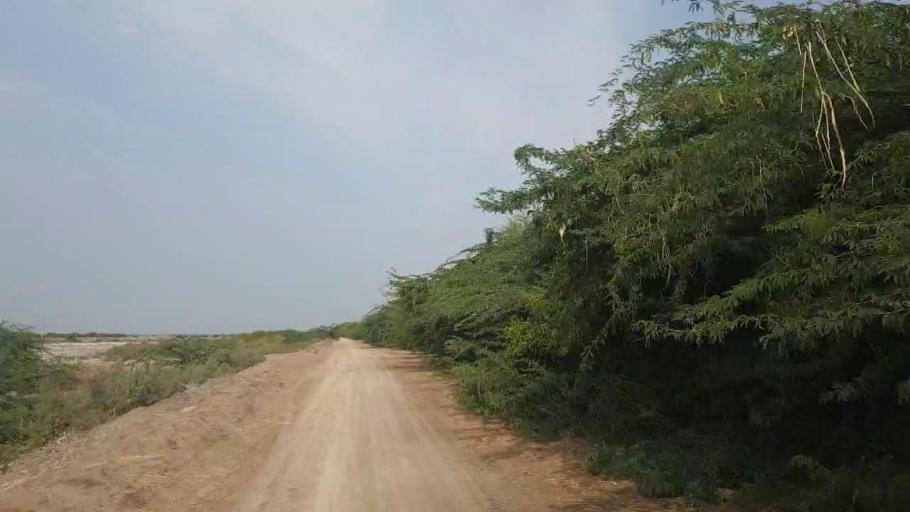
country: PK
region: Sindh
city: Badin
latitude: 24.5572
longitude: 68.7319
